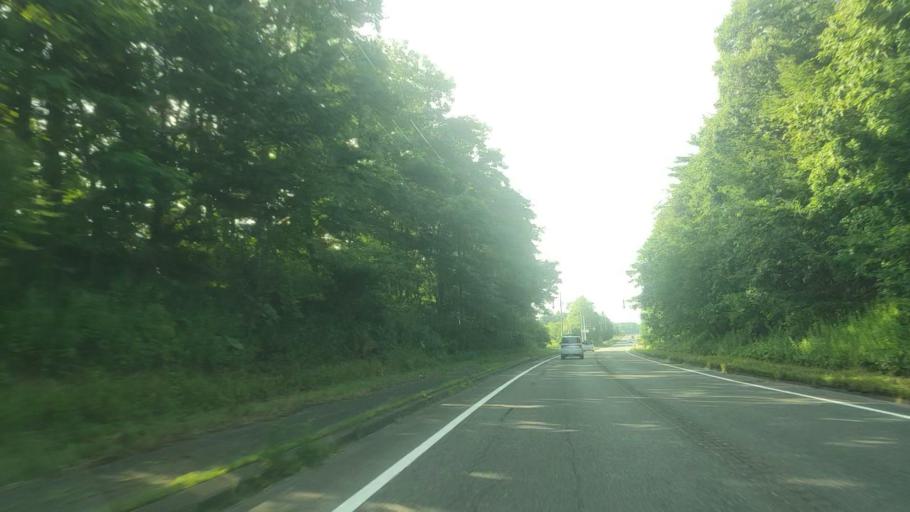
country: JP
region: Hokkaido
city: Chitose
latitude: 42.8787
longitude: 141.8164
